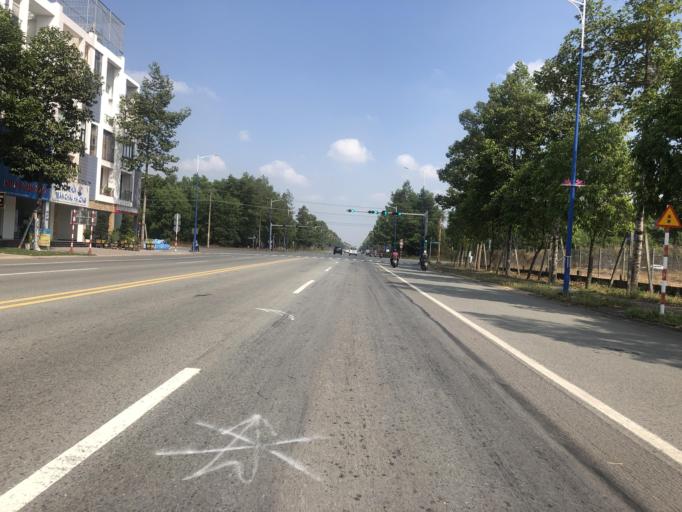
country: VN
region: Binh Duong
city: Thu Dau Mot
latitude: 11.0704
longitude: 106.6763
